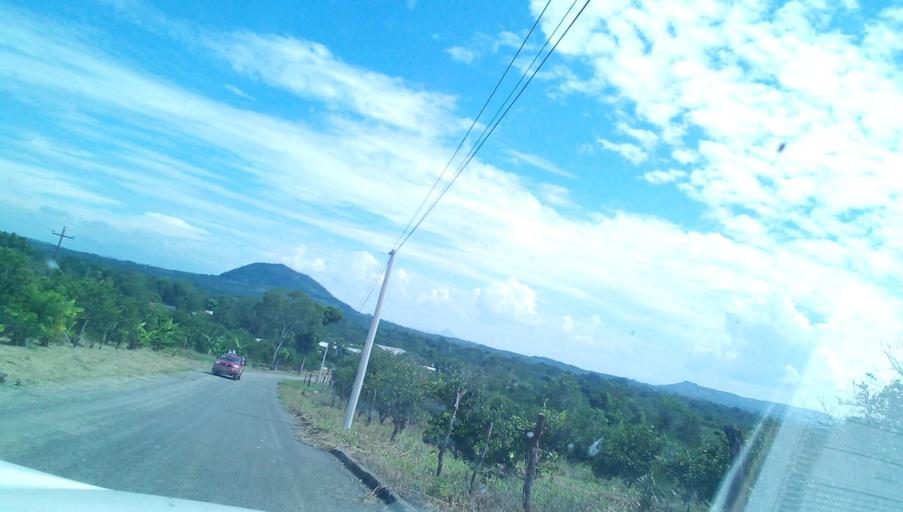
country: MX
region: Veracruz
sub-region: Alamo Temapache
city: Vegas de la Soledad y Soledad Dos
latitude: 20.8998
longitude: -97.9432
